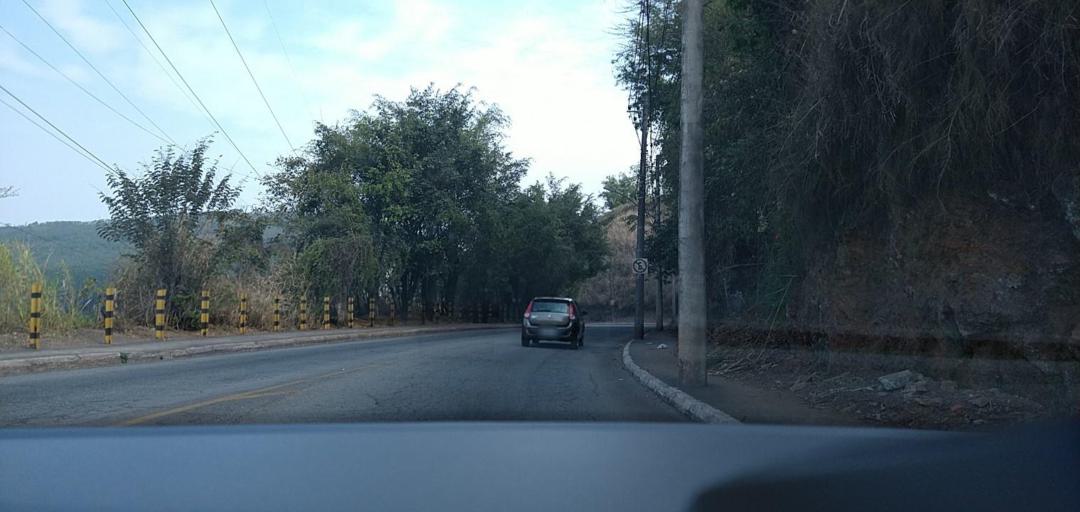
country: BR
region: Minas Gerais
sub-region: Joao Monlevade
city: Joao Monlevade
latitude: -19.8190
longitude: -43.1341
